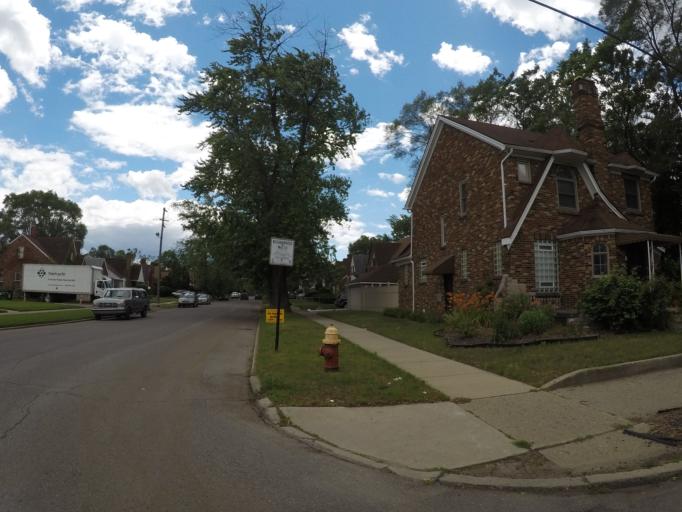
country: US
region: Michigan
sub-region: Oakland County
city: Ferndale
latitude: 42.4314
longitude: -83.1471
